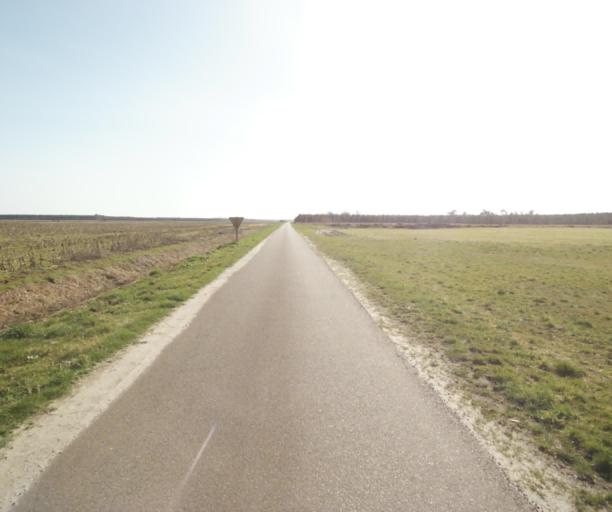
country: FR
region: Aquitaine
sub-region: Departement des Landes
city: Roquefort
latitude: 44.1800
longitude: -0.2527
